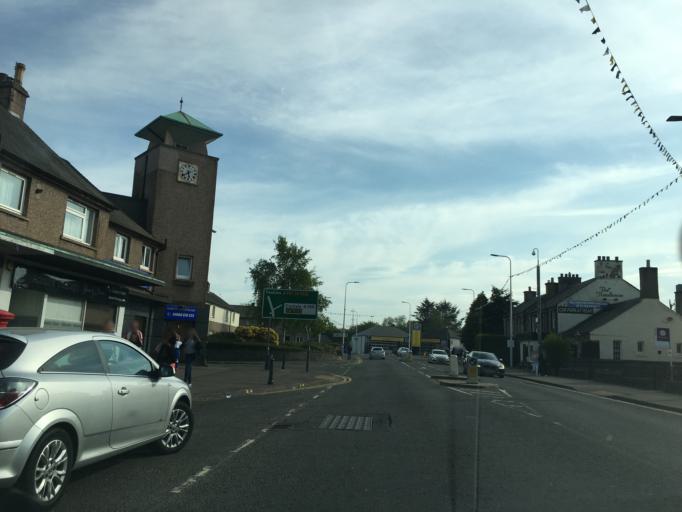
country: GB
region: Scotland
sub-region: Midlothian
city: Penicuik
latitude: 55.8326
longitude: -3.2233
